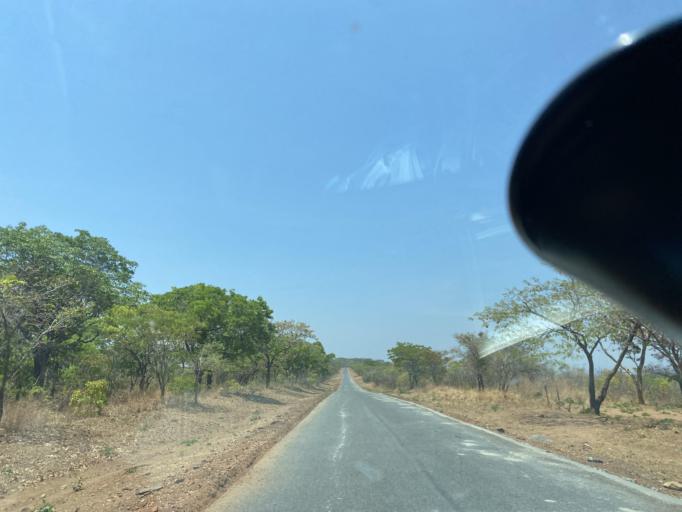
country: ZM
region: Lusaka
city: Kafue
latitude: -15.8447
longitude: 28.4126
